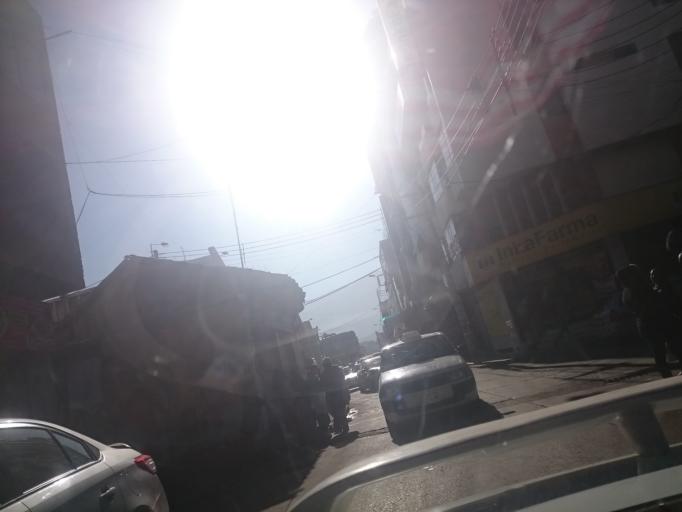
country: PE
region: Junin
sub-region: Provincia de Huancayo
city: Huancayo
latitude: -12.0723
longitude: -75.2058
